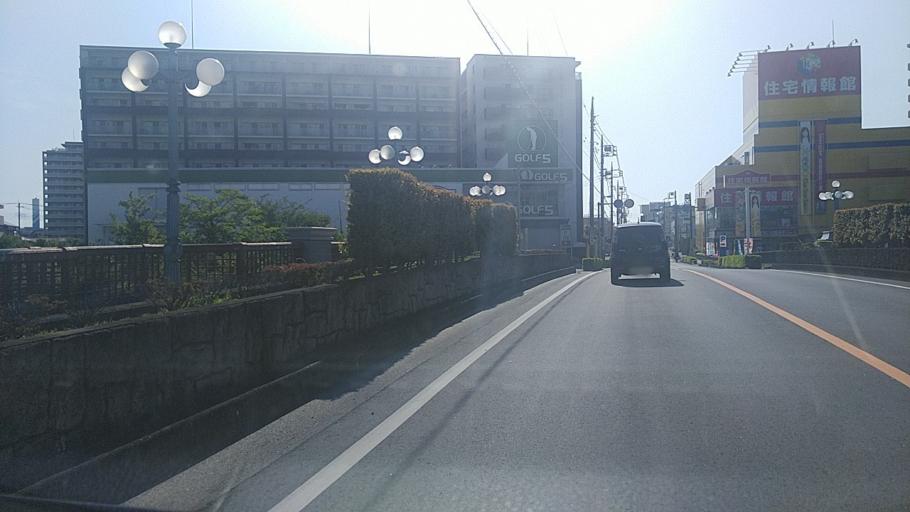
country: JP
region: Saitama
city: Kawaguchi
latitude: 35.8076
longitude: 139.7299
